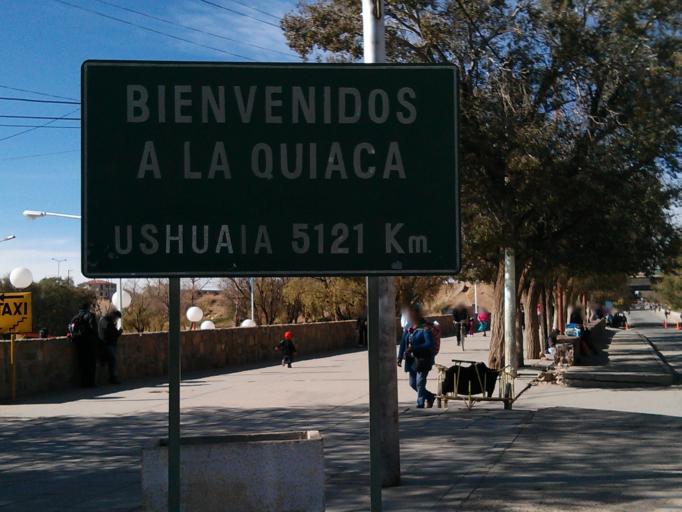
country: AR
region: Jujuy
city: La Quiaca
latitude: -22.0972
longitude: -65.5961
